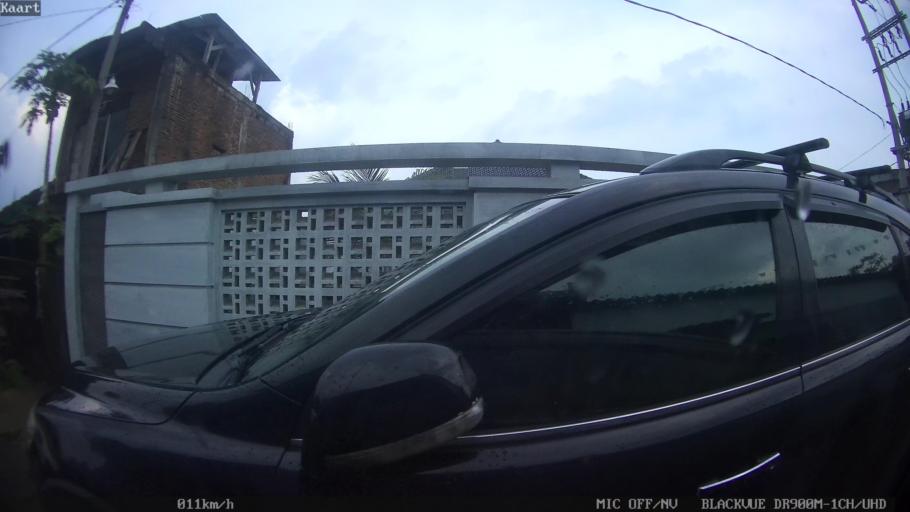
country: ID
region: Lampung
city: Bandarlampung
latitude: -5.4406
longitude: 105.2749
